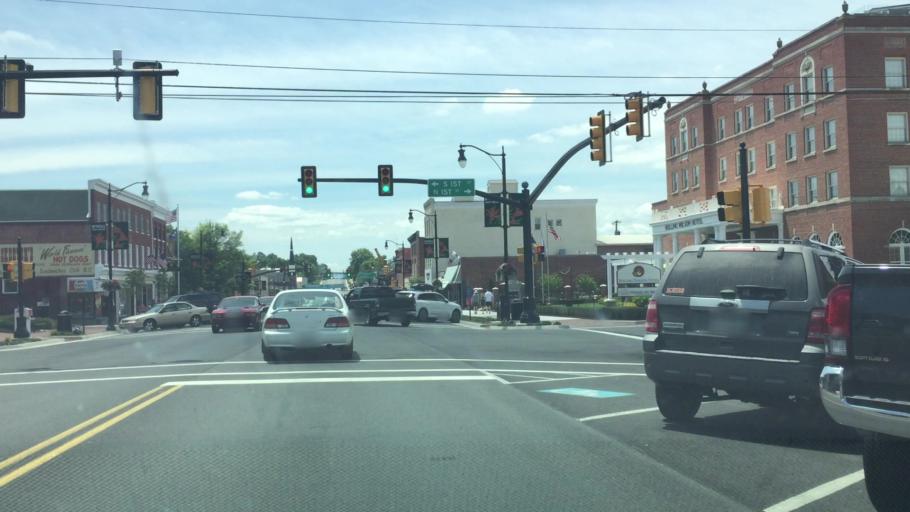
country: US
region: Virginia
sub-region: Wythe County
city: Wytheville
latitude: 36.9507
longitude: -81.0825
